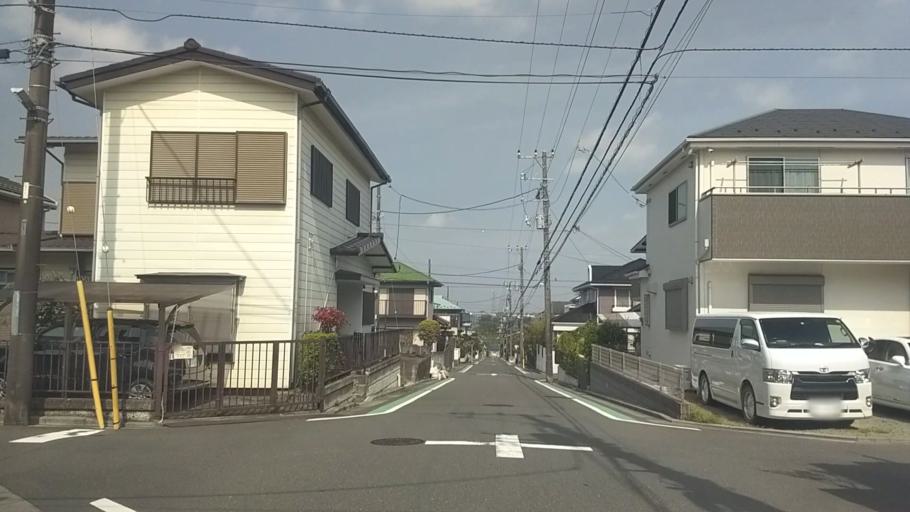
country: JP
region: Kanagawa
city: Yokohama
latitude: 35.3715
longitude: 139.6158
